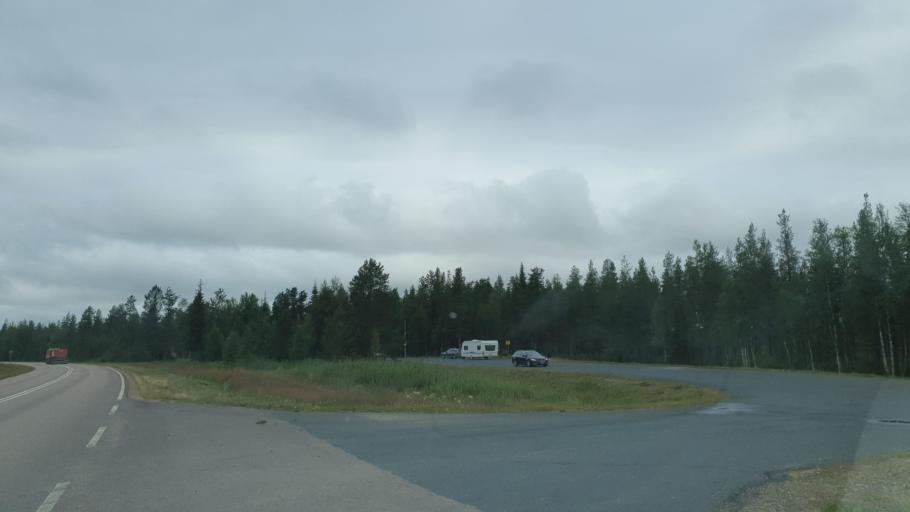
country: FI
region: Lapland
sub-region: Pohjois-Lappi
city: Sodankylae
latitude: 67.4232
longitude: 26.4410
